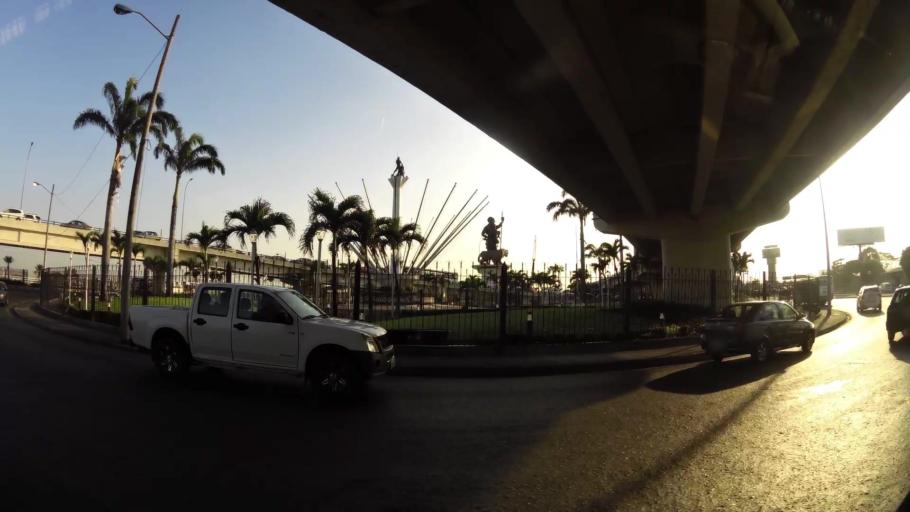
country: EC
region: Guayas
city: Eloy Alfaro
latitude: -2.1560
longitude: -79.8795
